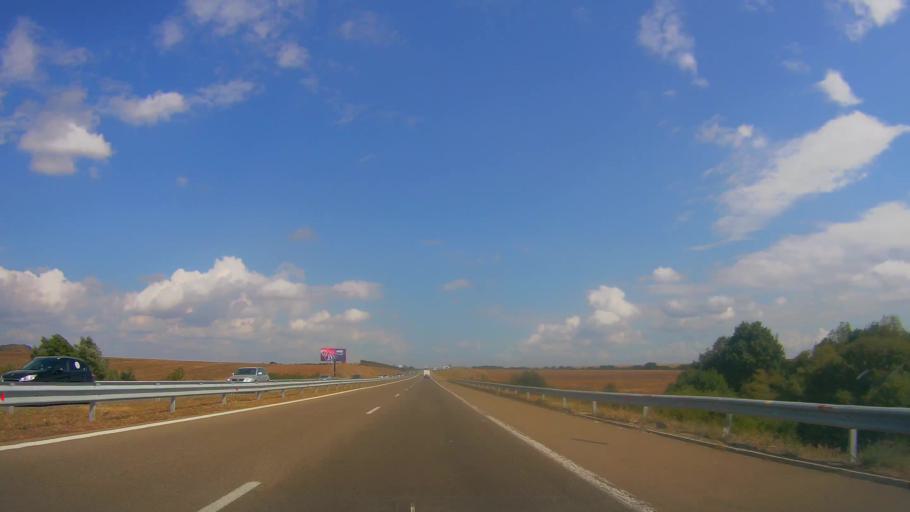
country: BG
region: Burgas
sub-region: Obshtina Karnobat
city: Karnobat
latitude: 42.5898
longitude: 27.0431
